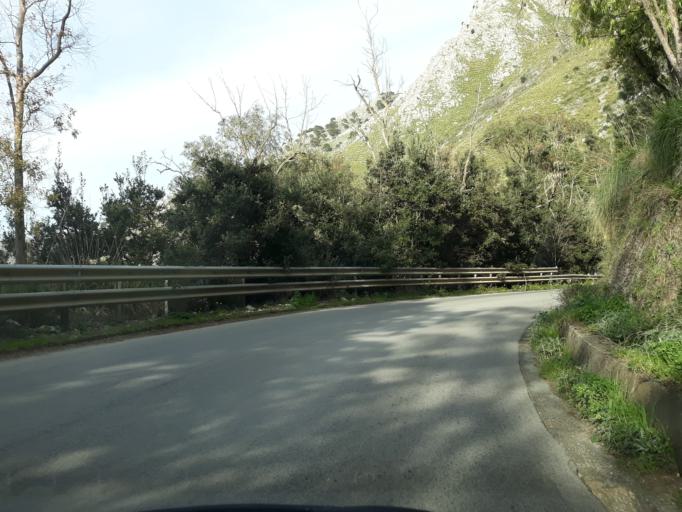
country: IT
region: Sicily
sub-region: Palermo
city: Torretta
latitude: 38.1124
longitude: 13.2392
